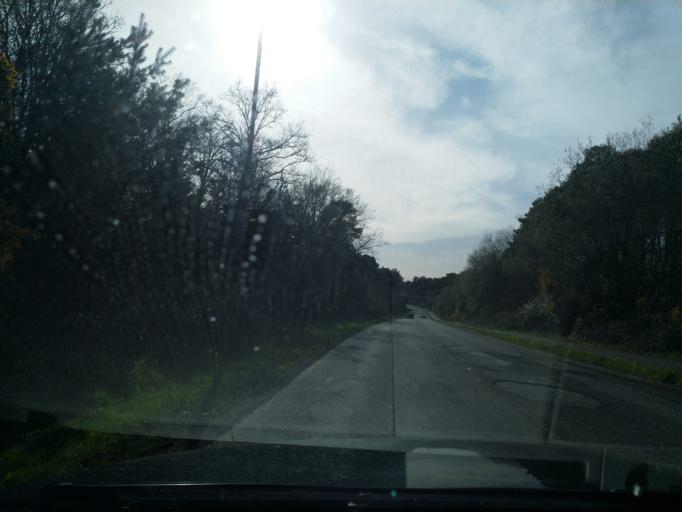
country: GB
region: England
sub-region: Hampshire
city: Fleet
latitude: 51.2834
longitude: -0.7965
